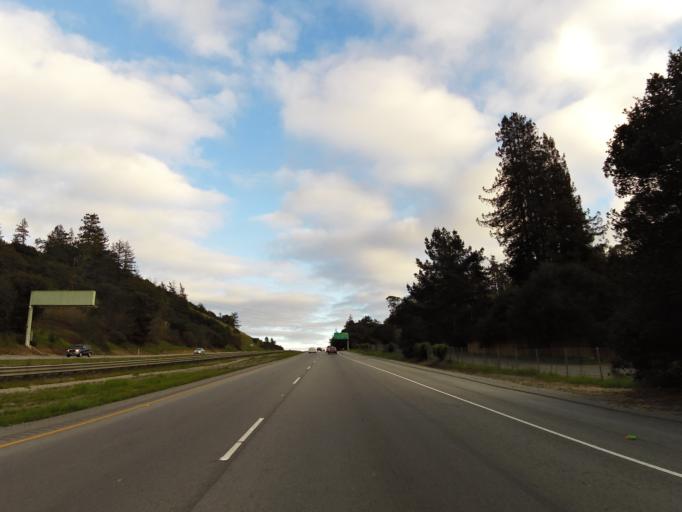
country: US
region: California
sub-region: Santa Cruz County
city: Rio Del Mar
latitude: 36.9682
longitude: -121.8706
